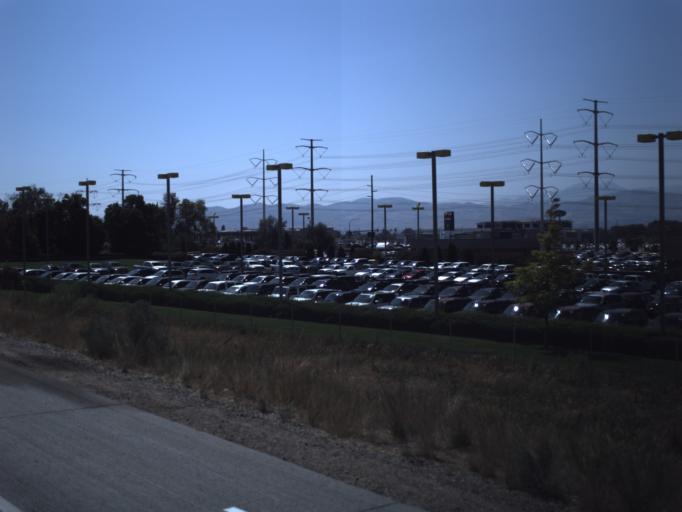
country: US
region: Utah
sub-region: Salt Lake County
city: White City
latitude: 40.5466
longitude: -111.8960
